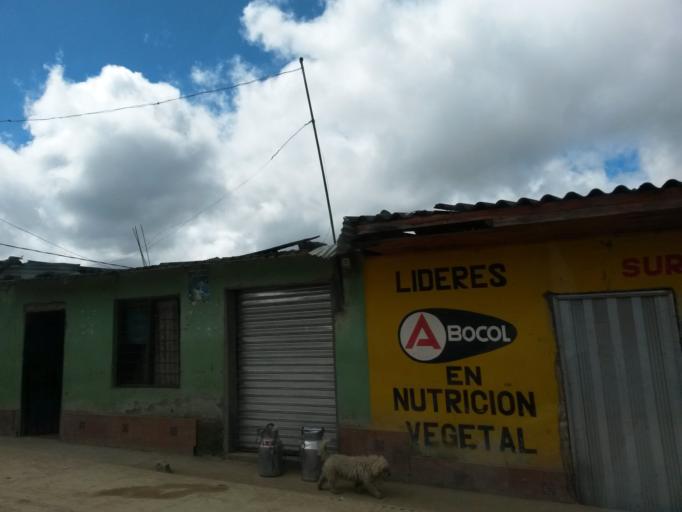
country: CO
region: Cauca
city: Totoro
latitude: 2.5118
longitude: -76.2886
